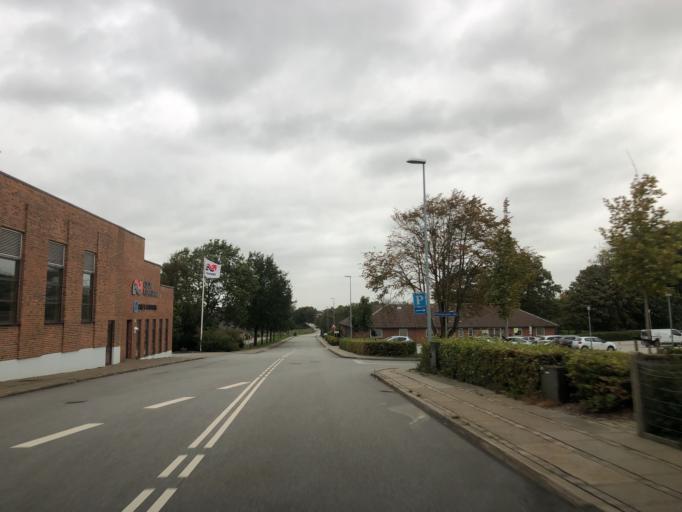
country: DK
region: Central Jutland
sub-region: Herning Kommune
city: Avlum
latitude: 56.2661
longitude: 8.7942
